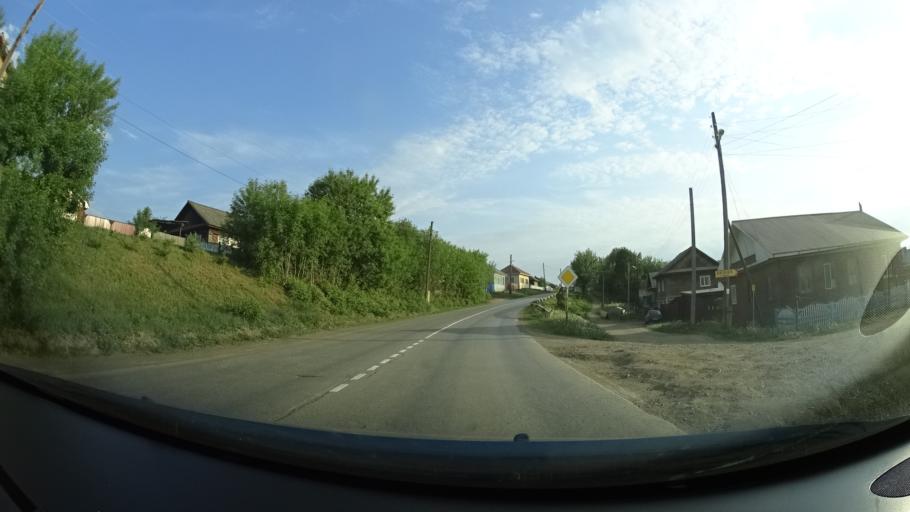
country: RU
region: Perm
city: Barda
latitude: 56.9317
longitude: 55.5926
